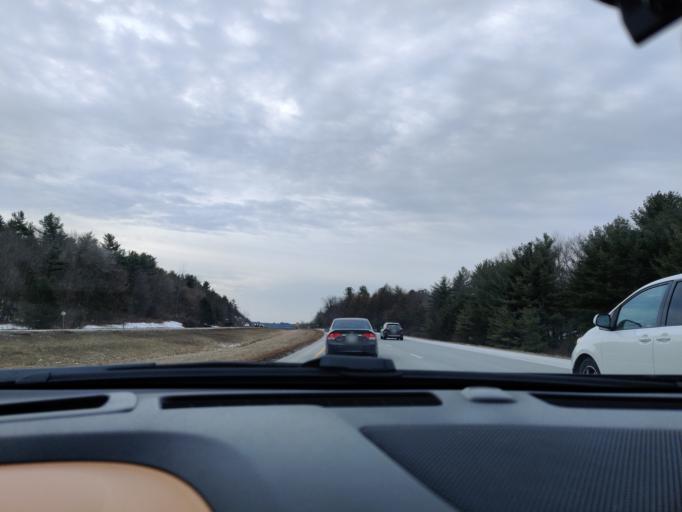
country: US
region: New York
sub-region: Jefferson County
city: Alexandria Bay
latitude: 44.4509
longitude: -75.8884
